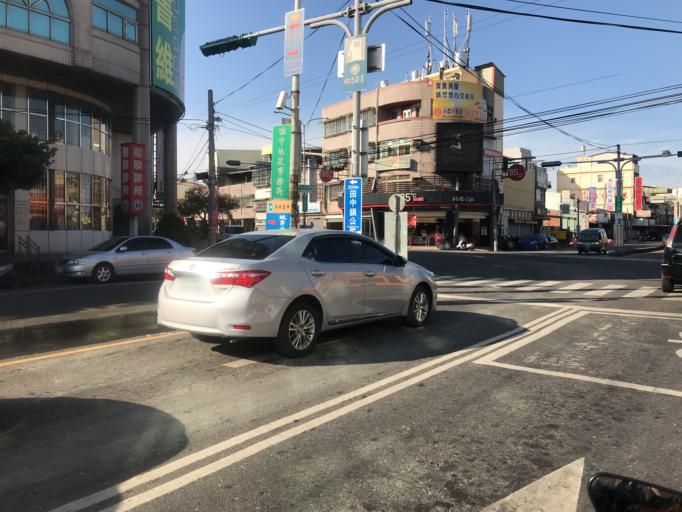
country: TW
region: Taiwan
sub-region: Nantou
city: Nantou
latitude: 23.8601
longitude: 120.5831
